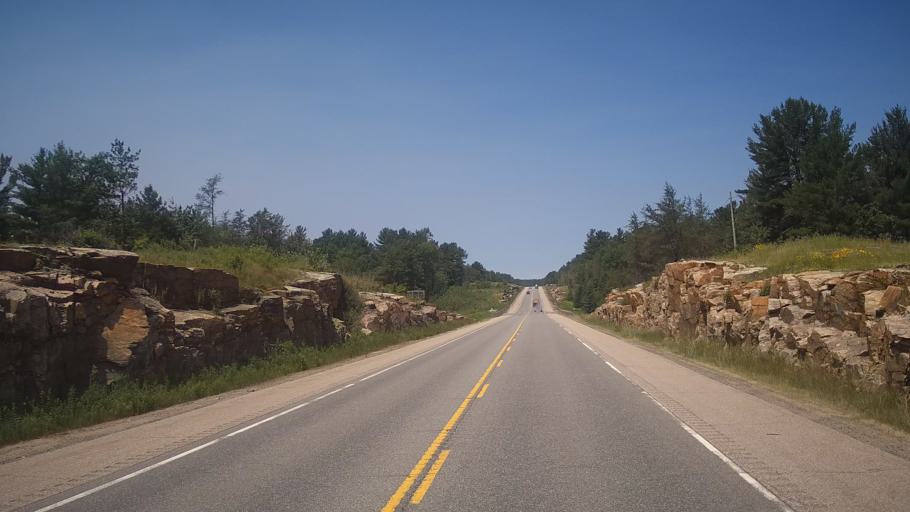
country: CA
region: Ontario
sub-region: Parry Sound District
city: Parry Sound
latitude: 45.4661
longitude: -80.1638
